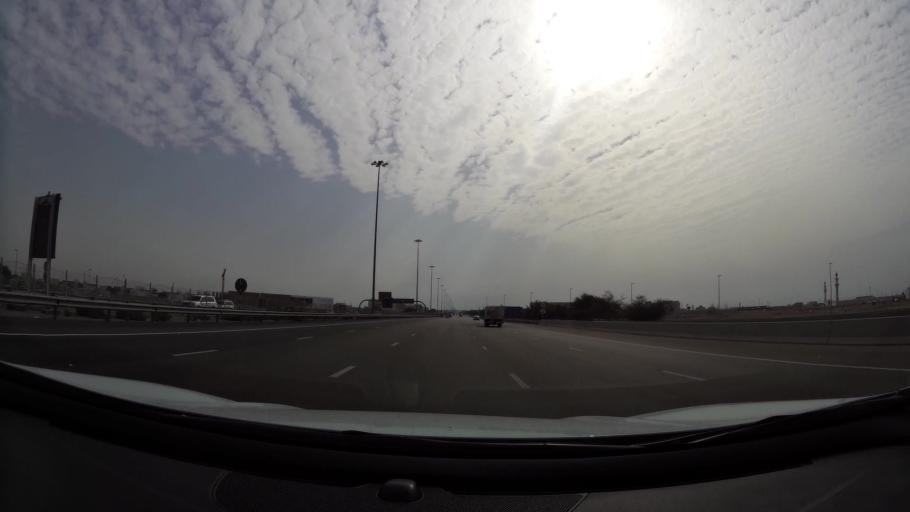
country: AE
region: Abu Dhabi
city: Abu Dhabi
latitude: 24.5384
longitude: 54.6848
